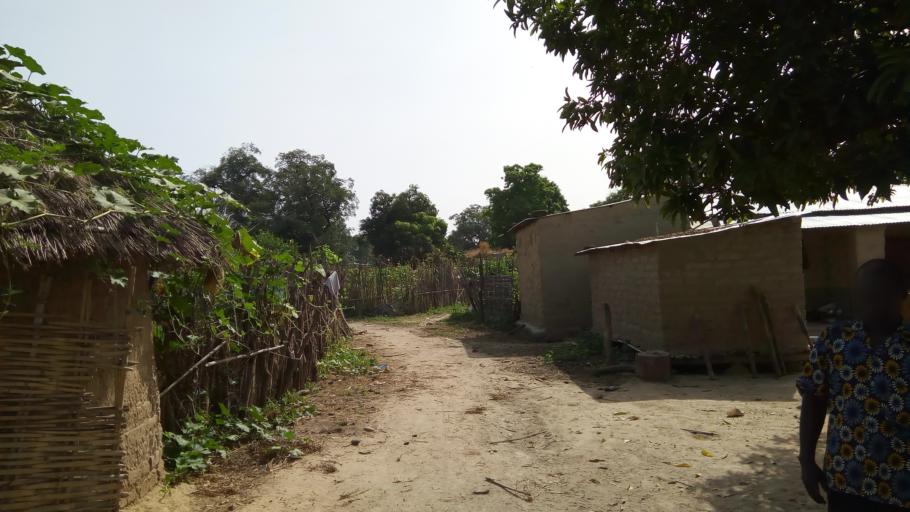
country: ML
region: Kayes
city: Kita
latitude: 13.1909
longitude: -8.7870
